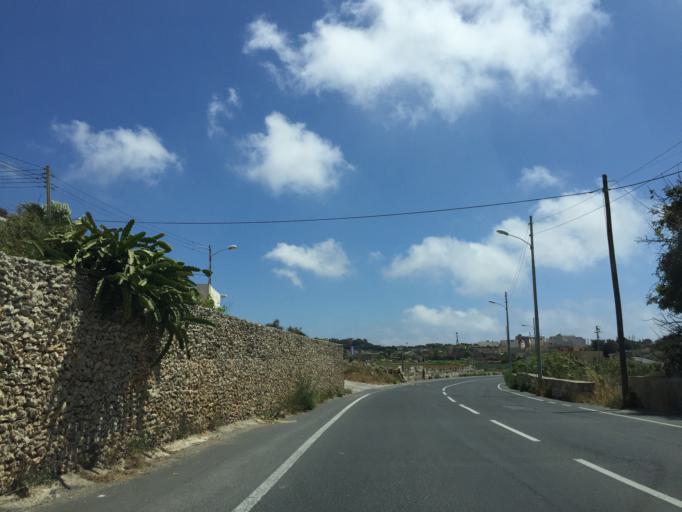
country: MT
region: Dingli
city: Dingli
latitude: 35.8684
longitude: 14.3908
